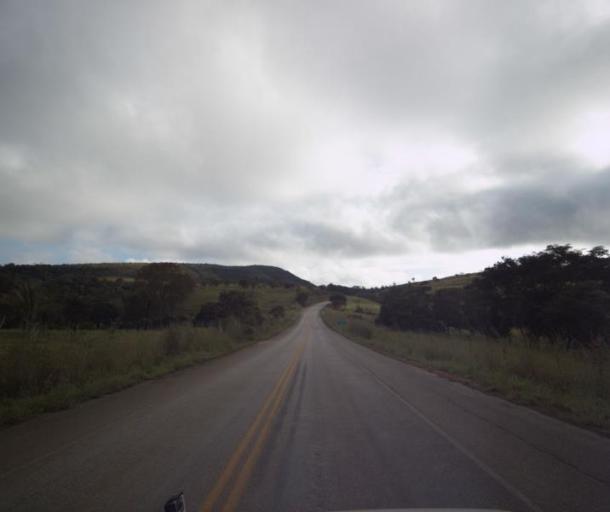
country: BR
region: Goias
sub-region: Pirenopolis
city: Pirenopolis
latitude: -15.7291
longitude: -48.7075
